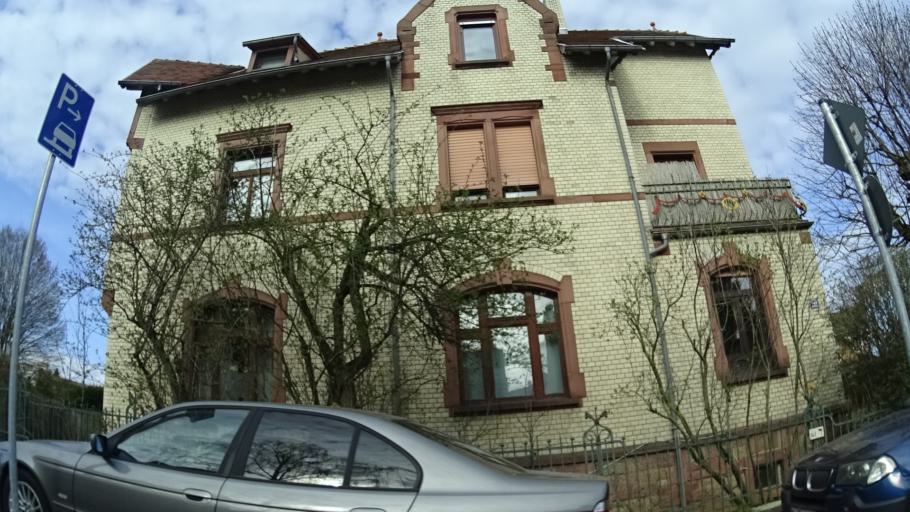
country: DE
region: Hesse
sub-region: Regierungsbezirk Darmstadt
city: Bad Vilbel
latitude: 50.1558
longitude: 8.7474
